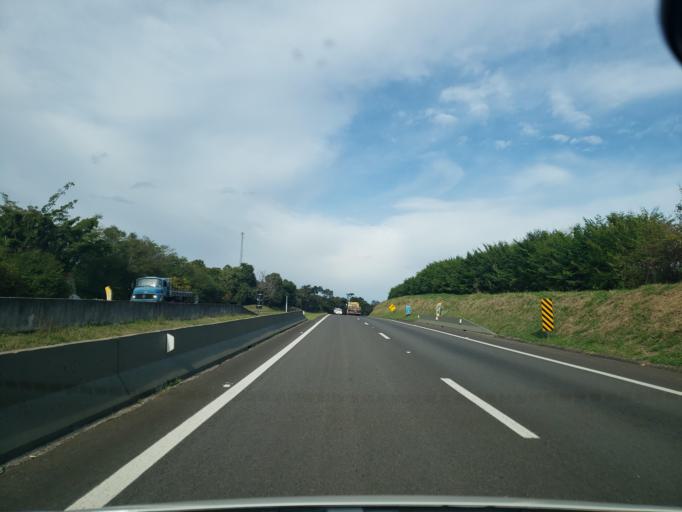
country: BR
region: Sao Paulo
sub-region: Brotas
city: Brotas
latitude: -22.2804
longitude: -47.9880
